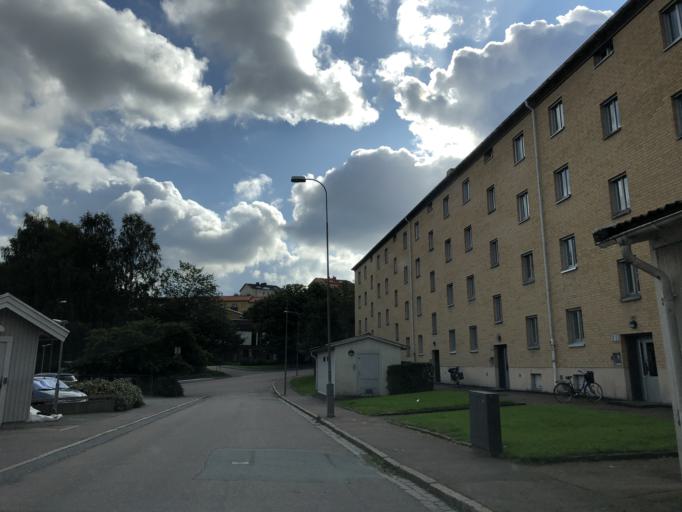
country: SE
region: Vaestra Goetaland
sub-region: Goteborg
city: Goeteborg
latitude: 57.7224
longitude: 12.0150
